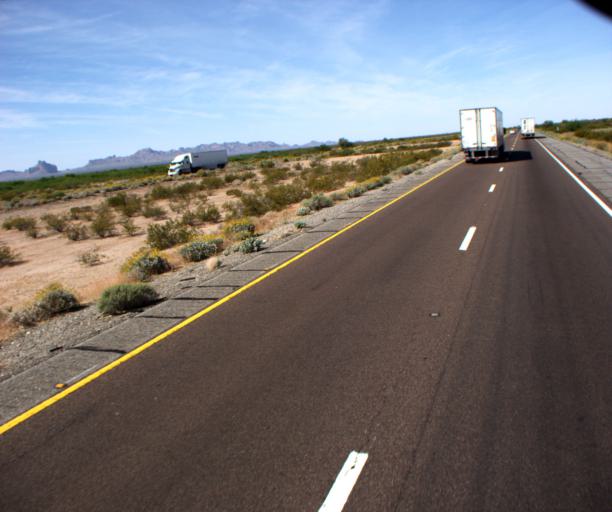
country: US
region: Arizona
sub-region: La Paz County
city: Salome
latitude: 33.5473
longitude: -113.2084
